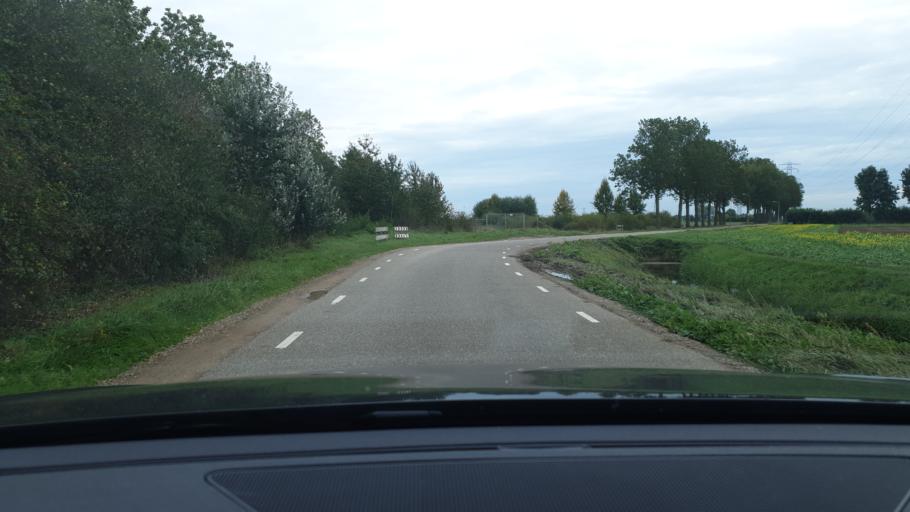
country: NL
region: Gelderland
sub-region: Gemeente Overbetuwe
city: Valburg
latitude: 51.8998
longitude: 5.7978
